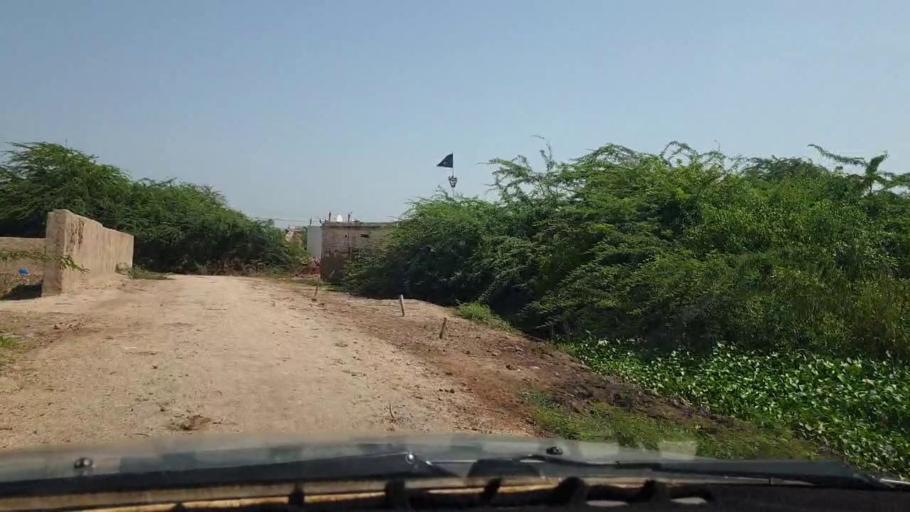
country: PK
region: Sindh
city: Tando Ghulam Ali
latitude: 25.1380
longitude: 68.8190
